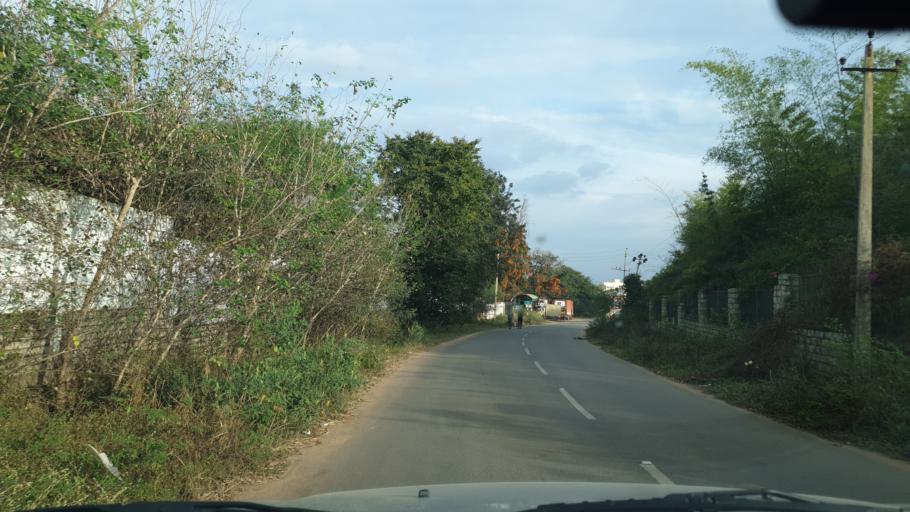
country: IN
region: Karnataka
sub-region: Bangalore Urban
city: Yelahanka
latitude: 13.1918
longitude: 77.6242
